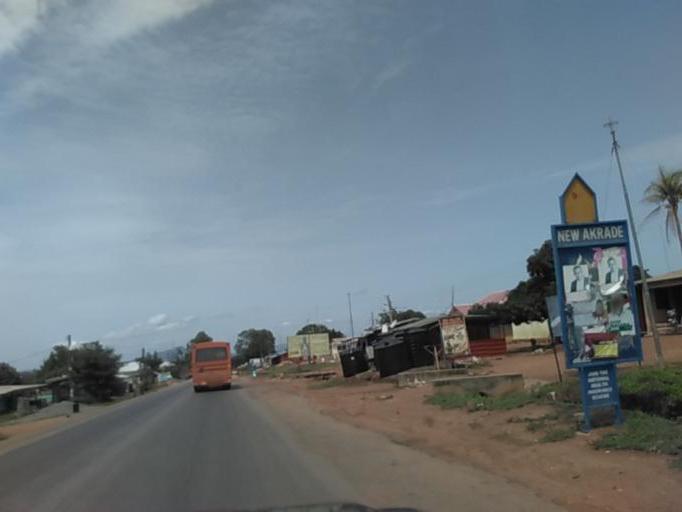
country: GH
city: Akropong
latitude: 6.2027
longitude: 0.0788
